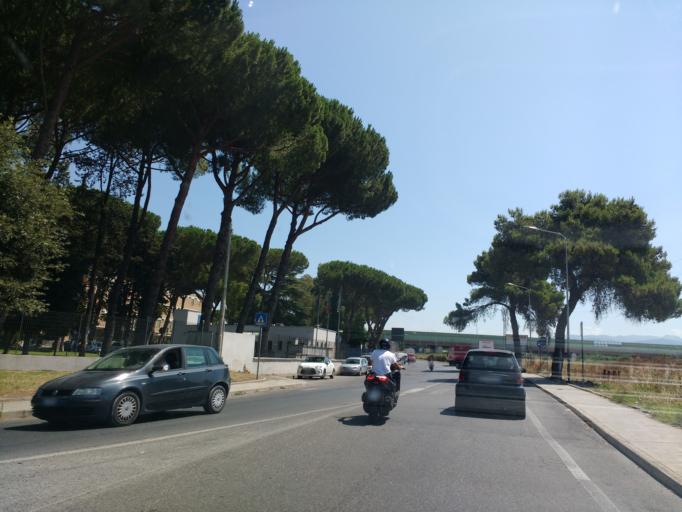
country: IT
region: Latium
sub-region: Citta metropolitana di Roma Capitale
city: Albuccione
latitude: 41.9520
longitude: 12.6981
